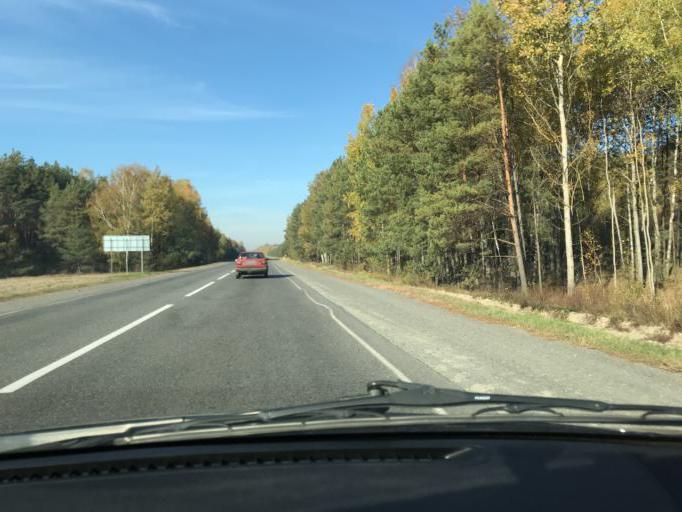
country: BY
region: Brest
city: Luninyets
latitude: 52.2645
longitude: 27.0174
